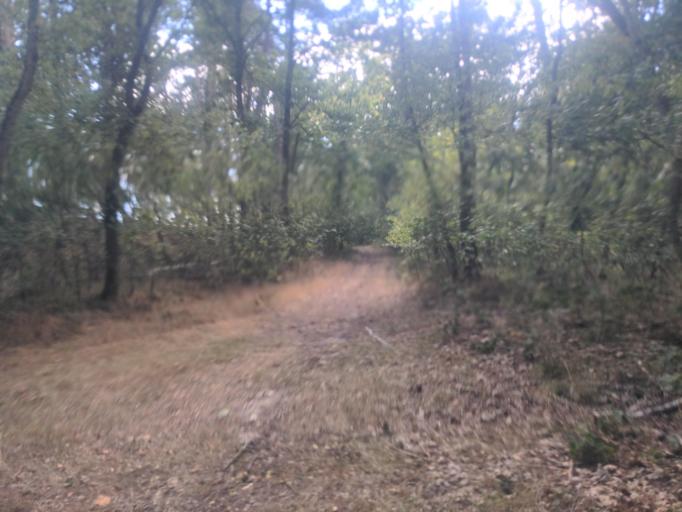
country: DE
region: Lower Saxony
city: Neu Darchau
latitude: 53.2126
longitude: 10.8725
